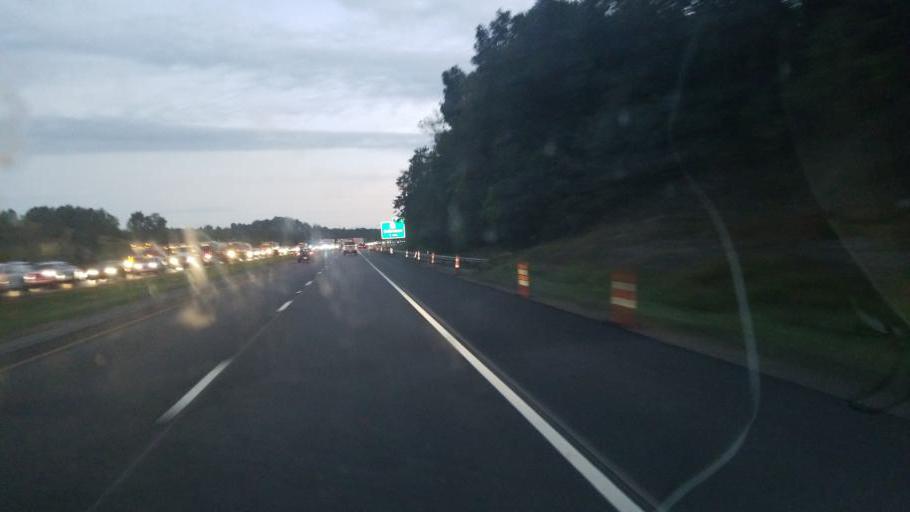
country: US
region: West Virginia
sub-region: Monongalia County
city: Brookhaven
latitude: 39.6013
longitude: -79.9307
